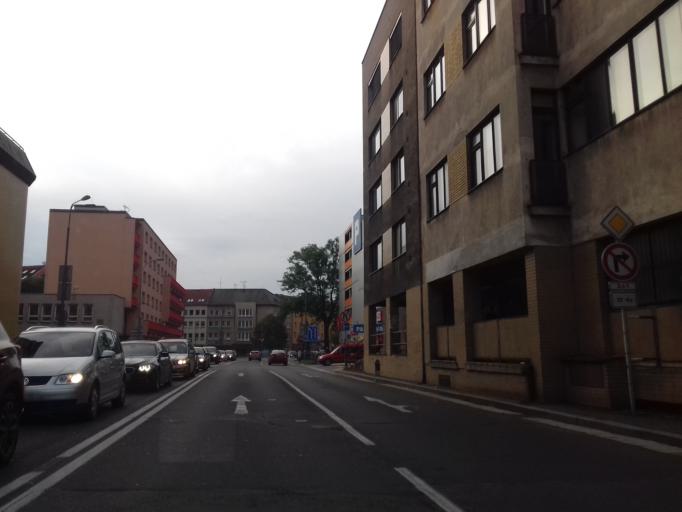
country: CZ
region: Pardubicky
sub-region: Okres Pardubice
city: Pardubice
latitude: 50.0369
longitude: 15.7792
